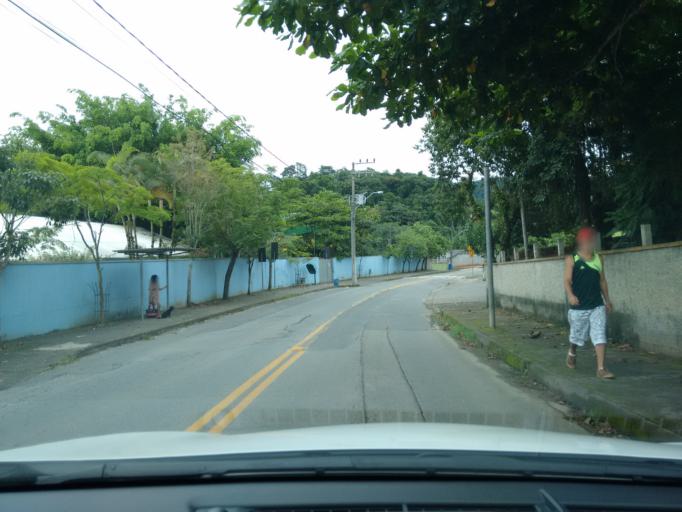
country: BR
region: Santa Catarina
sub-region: Blumenau
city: Blumenau
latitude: -26.8592
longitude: -49.1377
